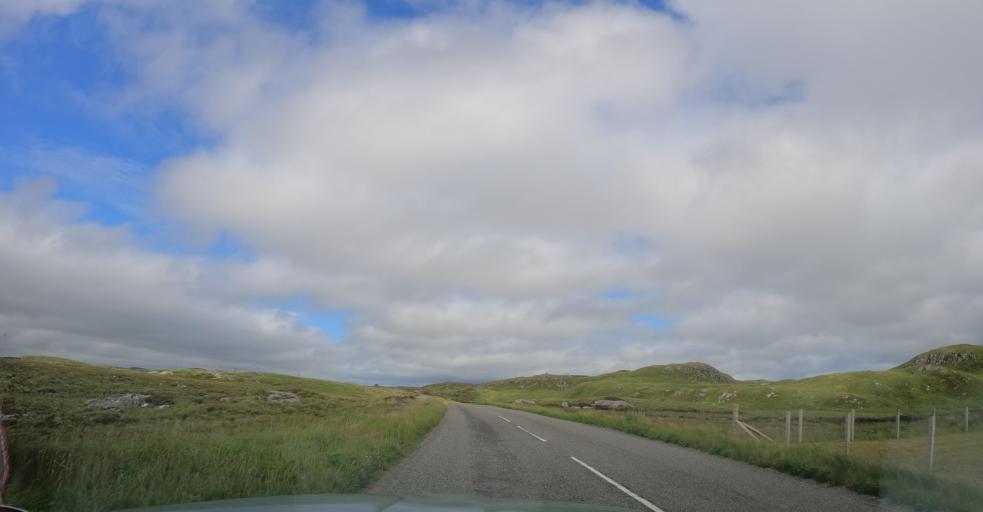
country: GB
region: Scotland
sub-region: Eilean Siar
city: Stornoway
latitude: 58.1081
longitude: -6.5122
